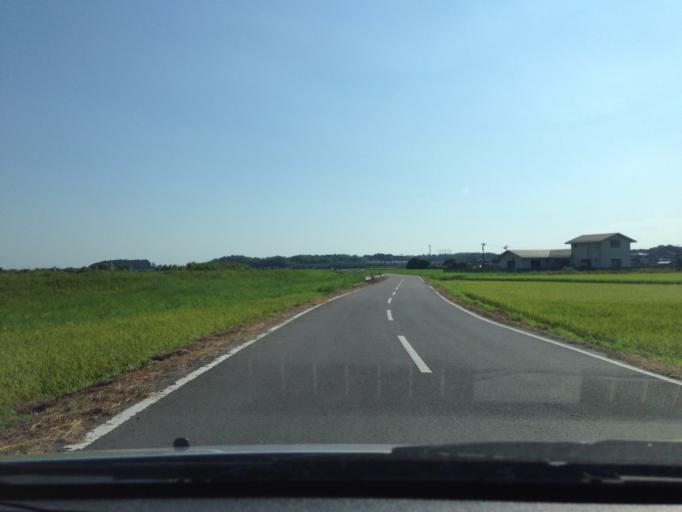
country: JP
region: Ibaraki
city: Inashiki
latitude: 35.9925
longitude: 140.3480
